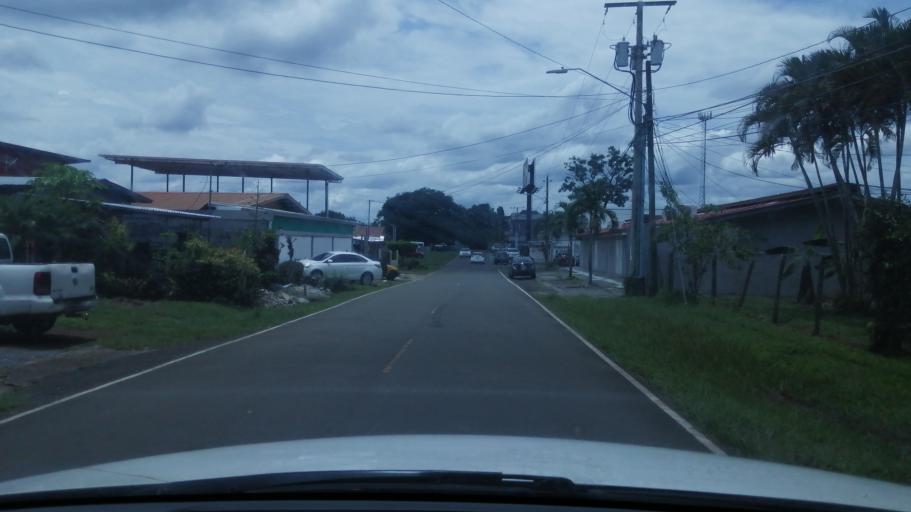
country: PA
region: Chiriqui
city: Mata del Nance
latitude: 8.4493
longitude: -82.4231
